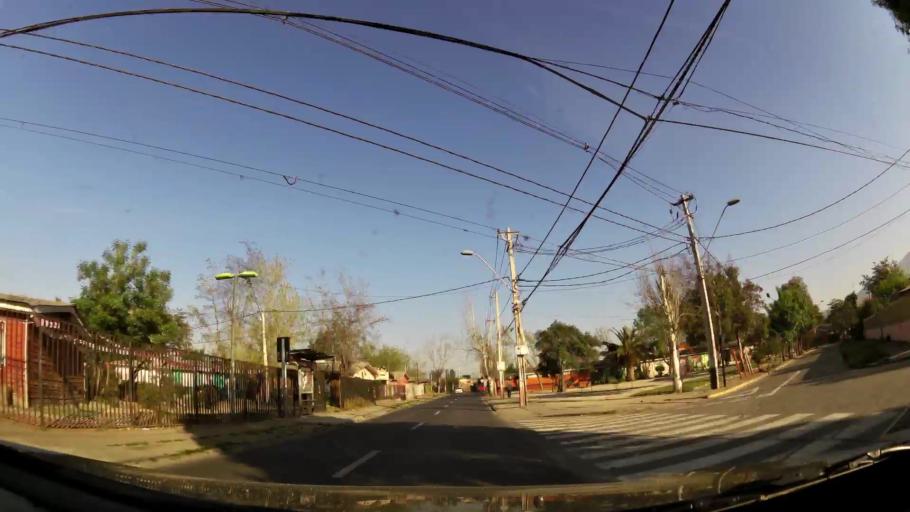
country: CL
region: Santiago Metropolitan
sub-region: Provincia de Santiago
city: Santiago
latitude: -33.3918
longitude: -70.6376
